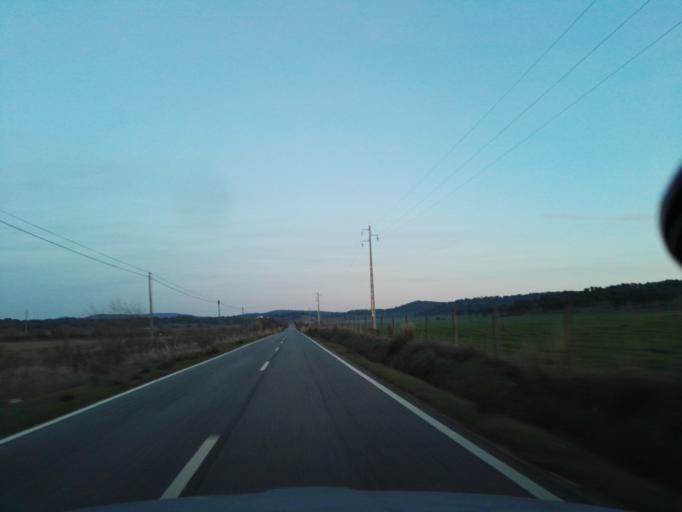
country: PT
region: Evora
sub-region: Arraiolos
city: Arraiolos
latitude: 38.7605
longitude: -8.1119
